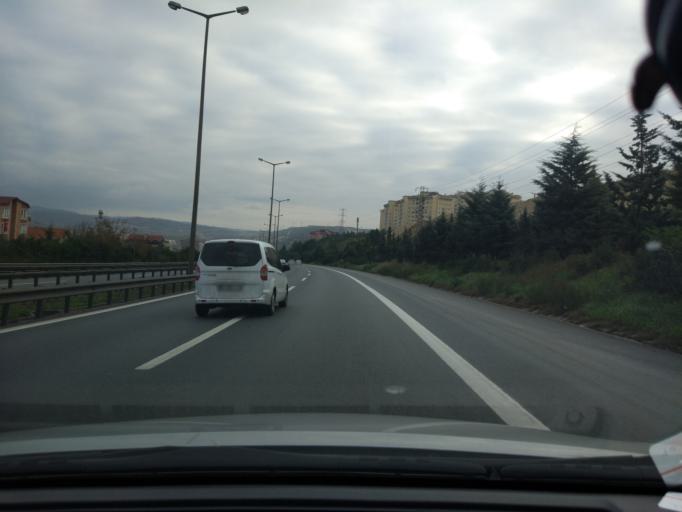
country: TR
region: Kocaeli
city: Izmit
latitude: 40.7851
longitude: 29.9601
